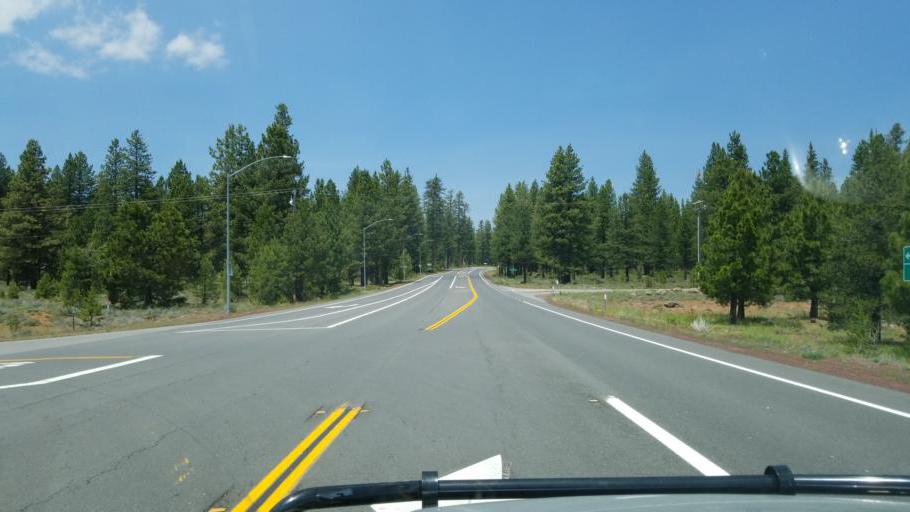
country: US
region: California
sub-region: Lassen County
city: Westwood
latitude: 40.5856
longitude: -121.0880
